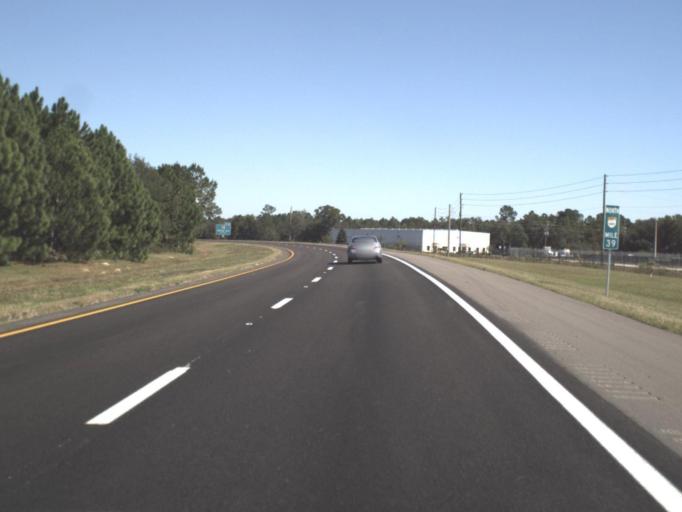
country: US
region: Florida
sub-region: Hernando County
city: Masaryktown
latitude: 28.4575
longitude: -82.4802
